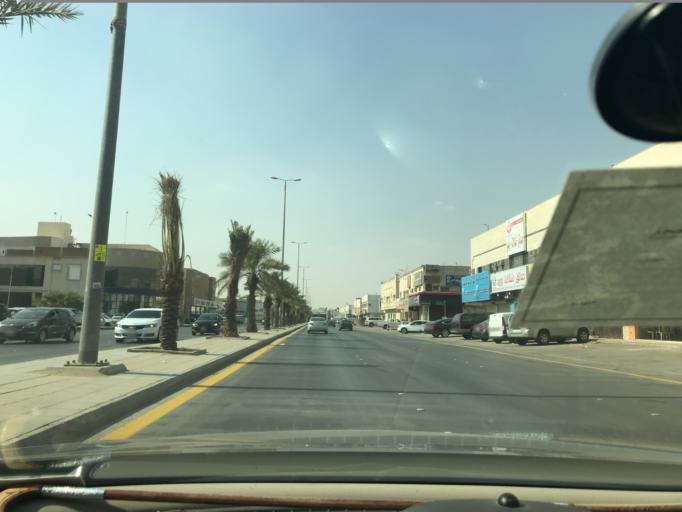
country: SA
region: Ar Riyad
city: Riyadh
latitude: 24.7405
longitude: 46.7589
